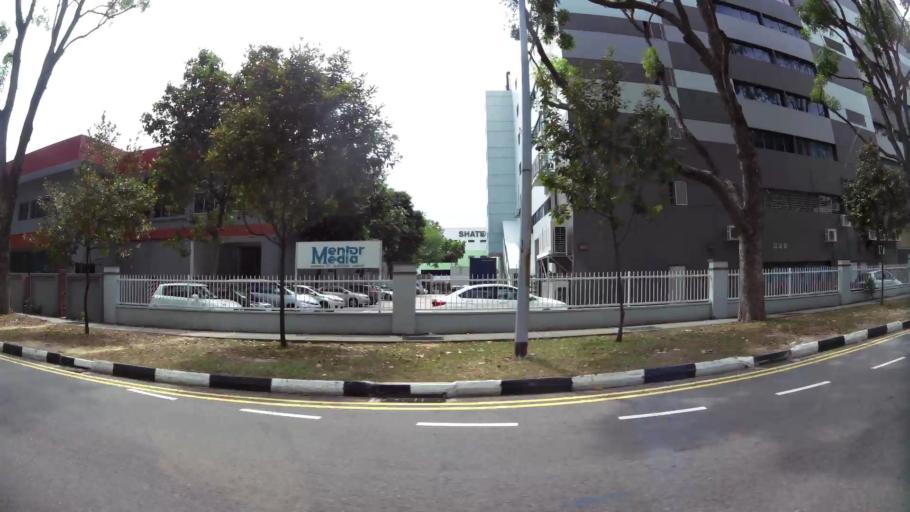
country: SG
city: Singapore
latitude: 1.3451
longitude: 103.7499
